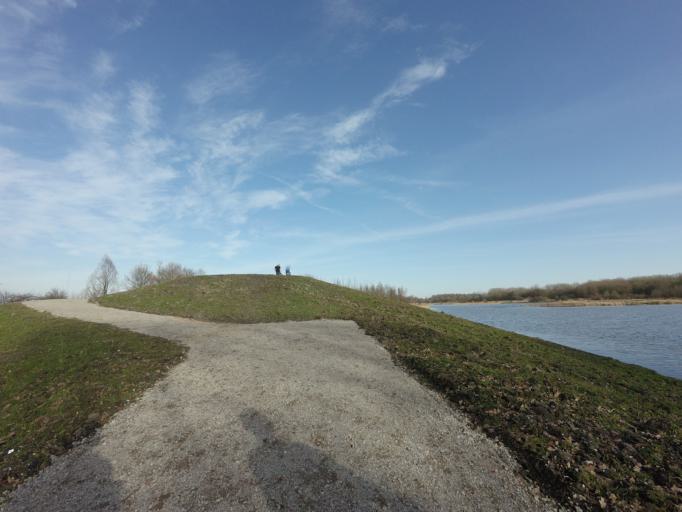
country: NL
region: North Holland
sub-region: Gemeente Naarden
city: Naarden
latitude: 52.3385
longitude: 5.1736
